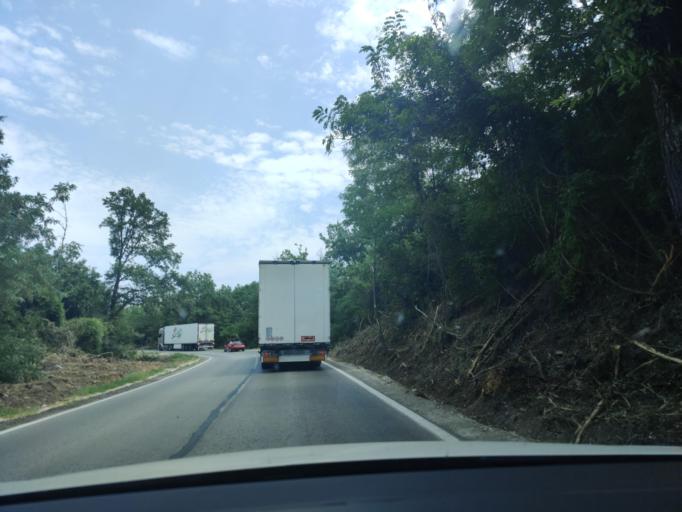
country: BG
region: Vidin
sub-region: Obshtina Ruzhintsi
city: Ruzhintsi
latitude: 43.6754
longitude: 22.7711
